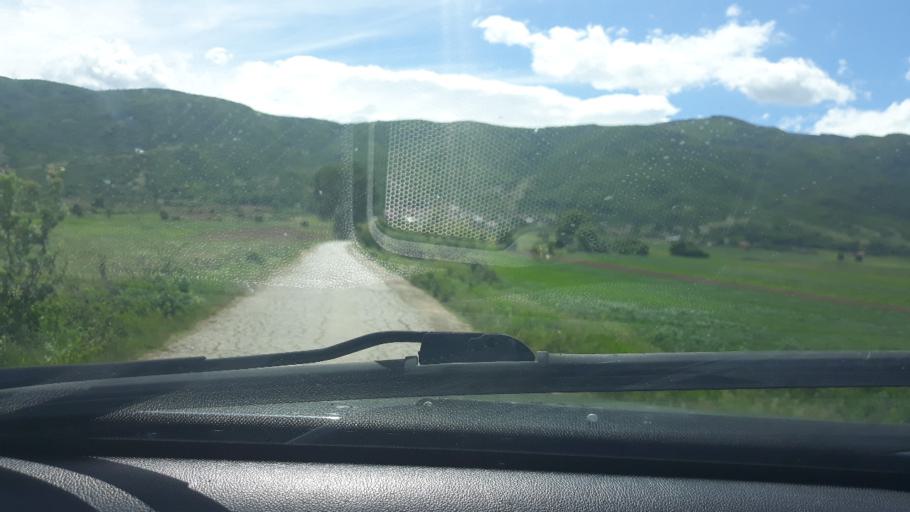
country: MK
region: Krivogastani
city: Krivogashtani
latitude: 41.3400
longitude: 21.3099
